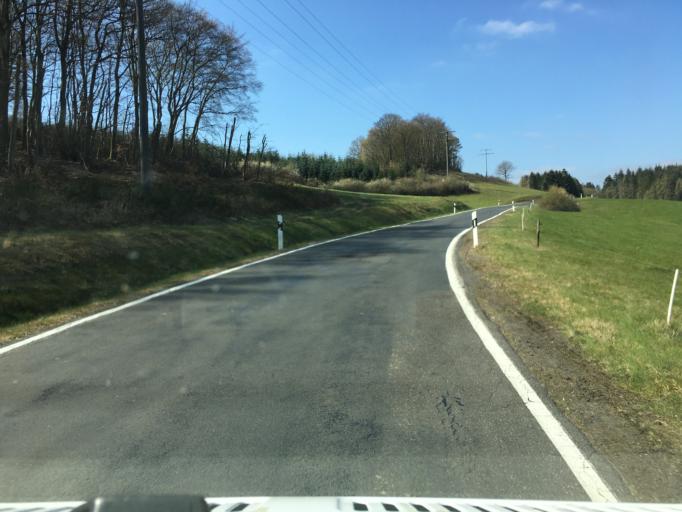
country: DE
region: Rheinland-Pfalz
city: Kirchsahr
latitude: 50.5102
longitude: 6.8963
